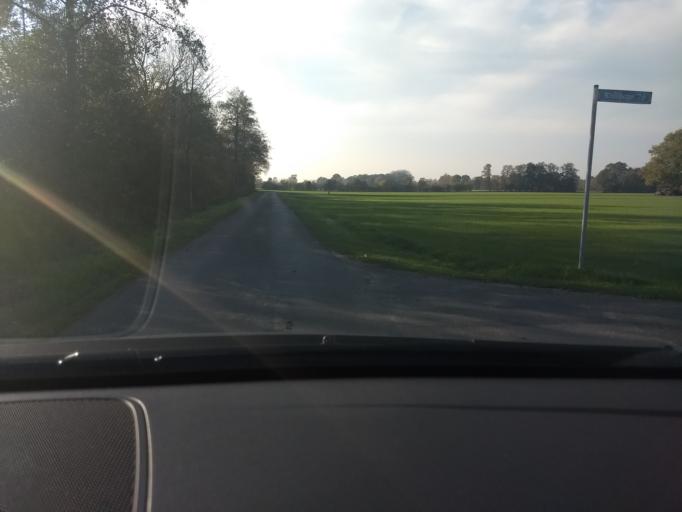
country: DE
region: North Rhine-Westphalia
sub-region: Regierungsbezirk Munster
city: Sudlohn
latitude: 51.9078
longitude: 6.8301
